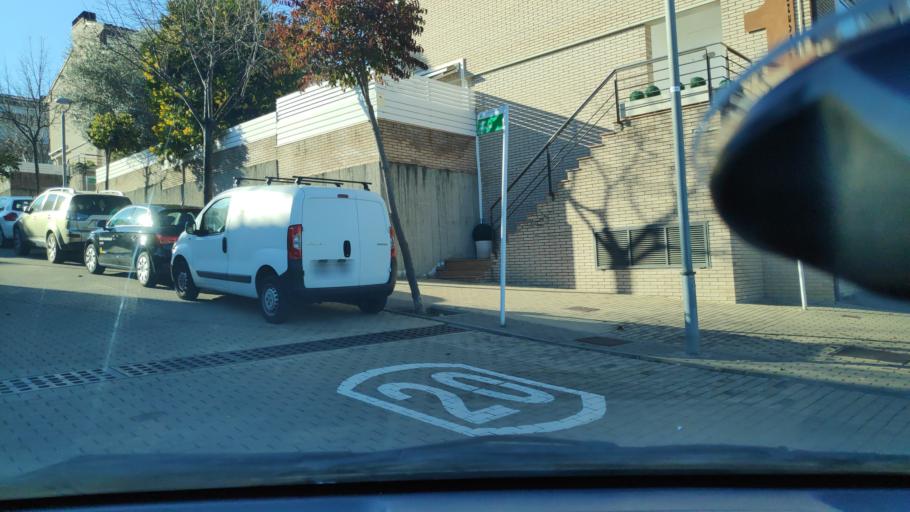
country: ES
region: Catalonia
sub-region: Provincia de Barcelona
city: Sant Quirze del Valles
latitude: 41.5307
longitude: 2.0712
